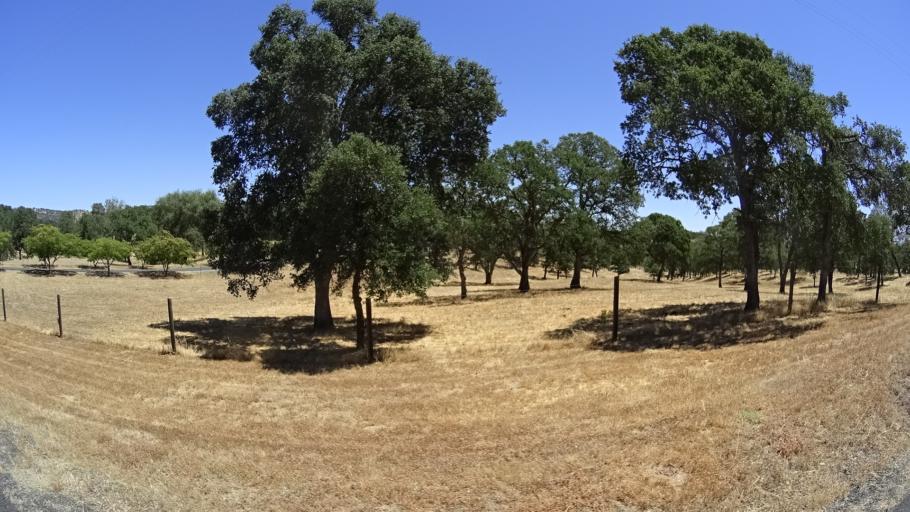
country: US
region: California
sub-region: Calaveras County
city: Copperopolis
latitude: 37.9697
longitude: -120.6748
